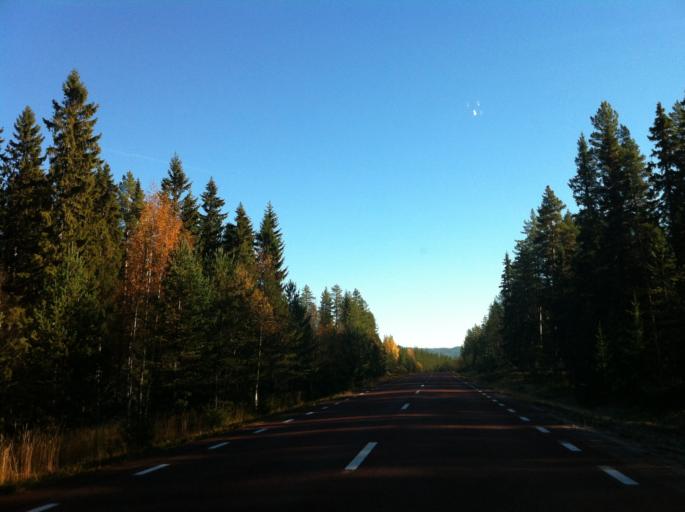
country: SE
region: Dalarna
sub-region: Alvdalens Kommun
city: AElvdalen
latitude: 61.3245
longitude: 13.6183
